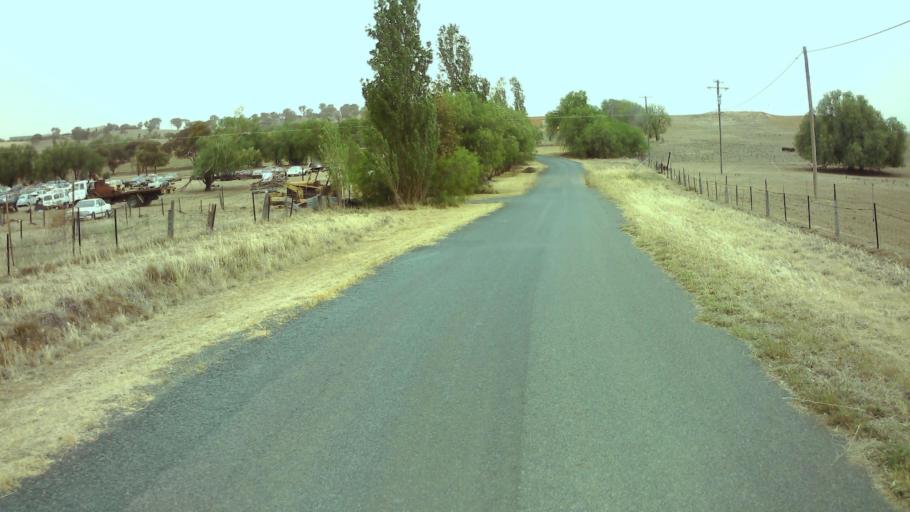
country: AU
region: New South Wales
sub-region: Weddin
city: Grenfell
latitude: -33.9059
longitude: 148.1699
